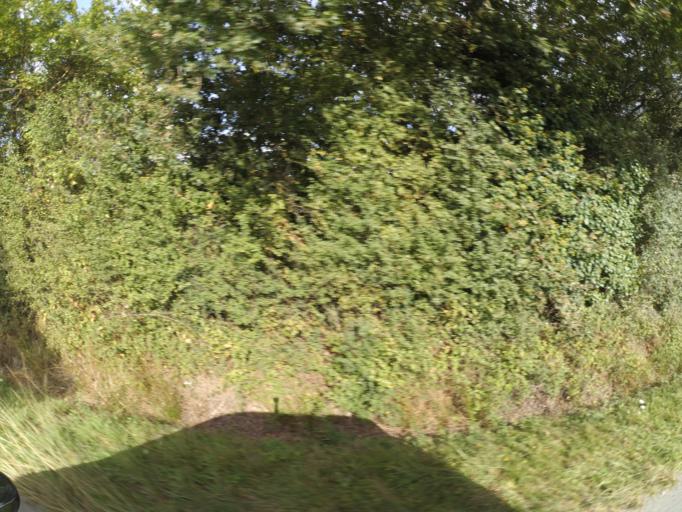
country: FR
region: Pays de la Loire
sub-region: Departement de la Loire-Atlantique
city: Casson
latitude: 47.4044
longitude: -1.5890
